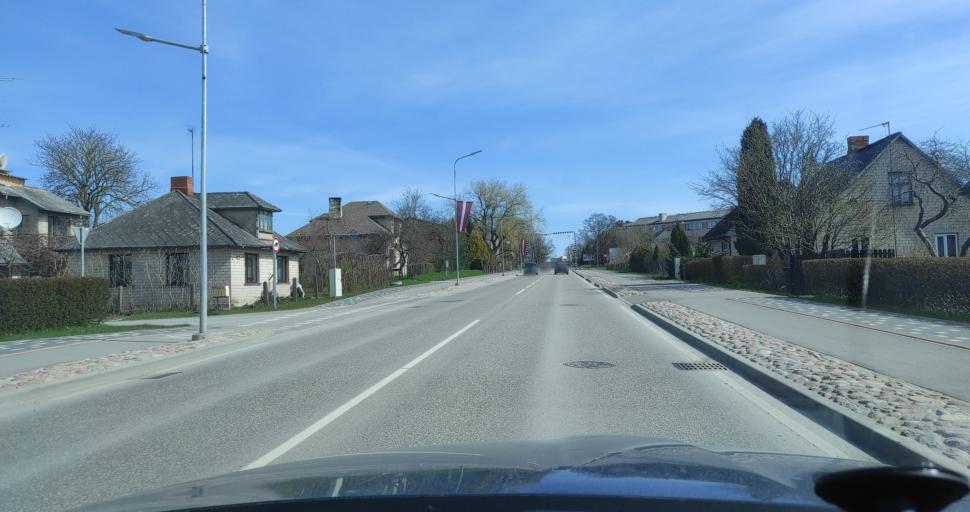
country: LV
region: Talsu Rajons
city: Talsi
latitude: 57.2404
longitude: 22.5774
